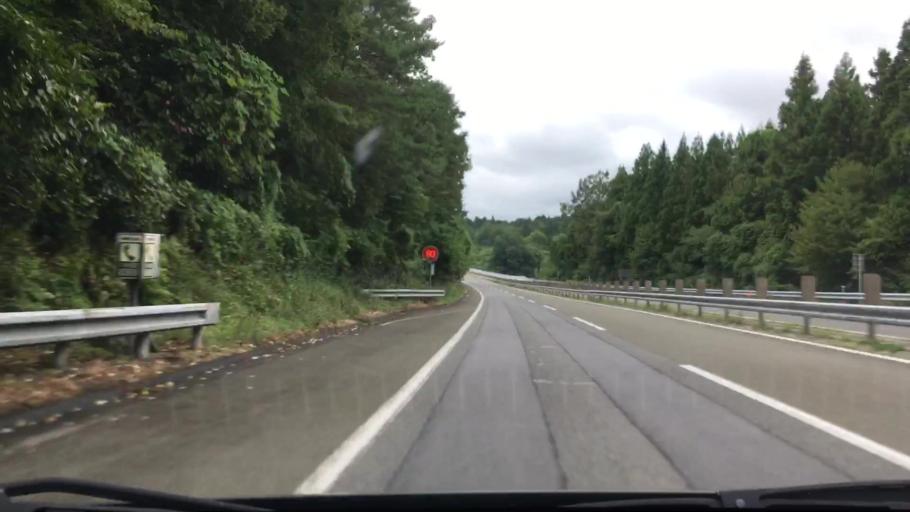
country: JP
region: Hiroshima
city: Miyoshi
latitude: 34.7972
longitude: 132.8920
